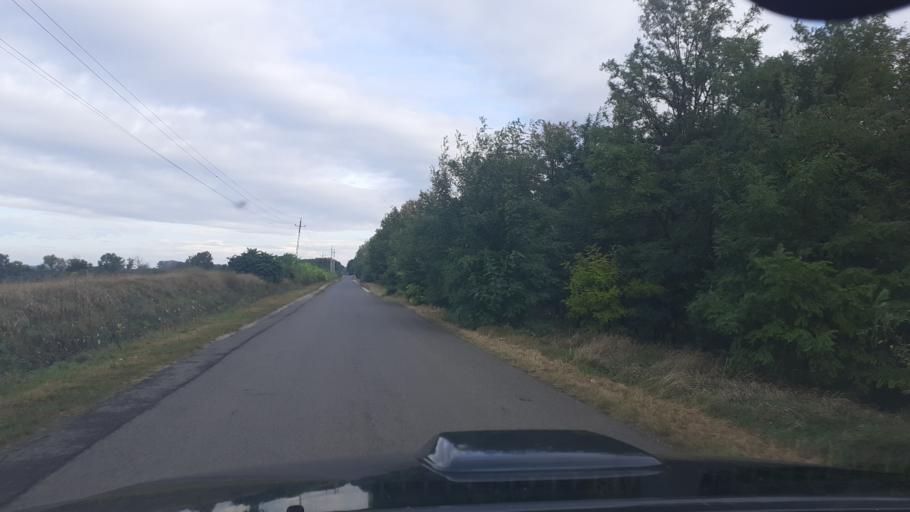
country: HU
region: Fejer
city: Baracs
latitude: 46.9331
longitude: 18.8709
